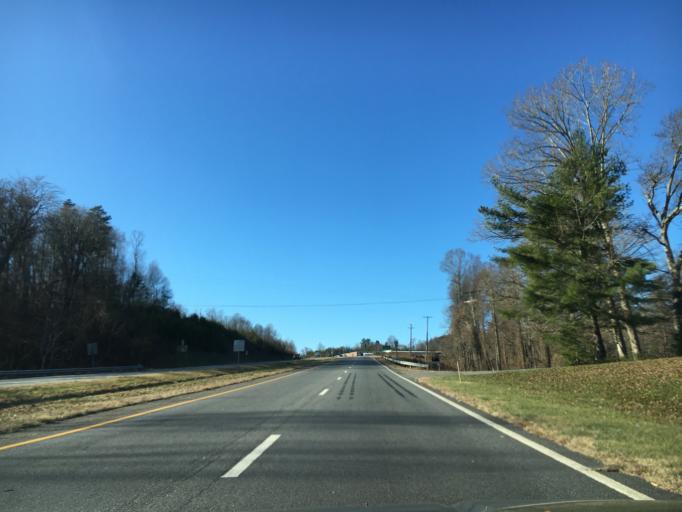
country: US
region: Virginia
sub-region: Patrick County
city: Patrick Springs
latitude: 36.6393
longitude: -80.2190
